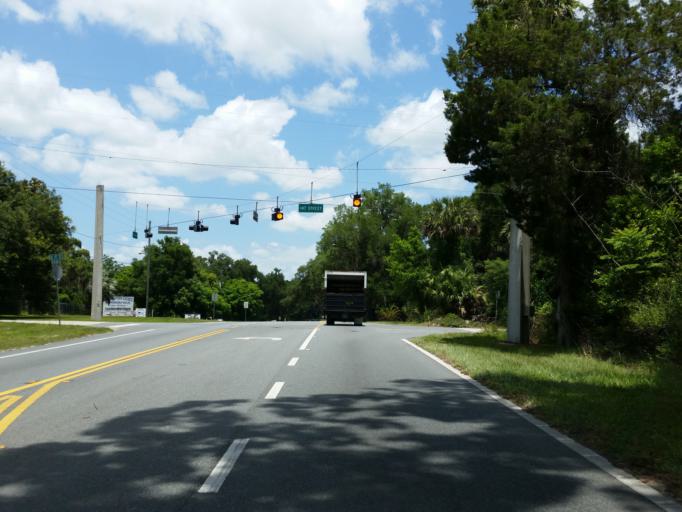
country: US
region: Florida
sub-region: Marion County
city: Belleview
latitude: 29.0083
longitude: -82.0413
